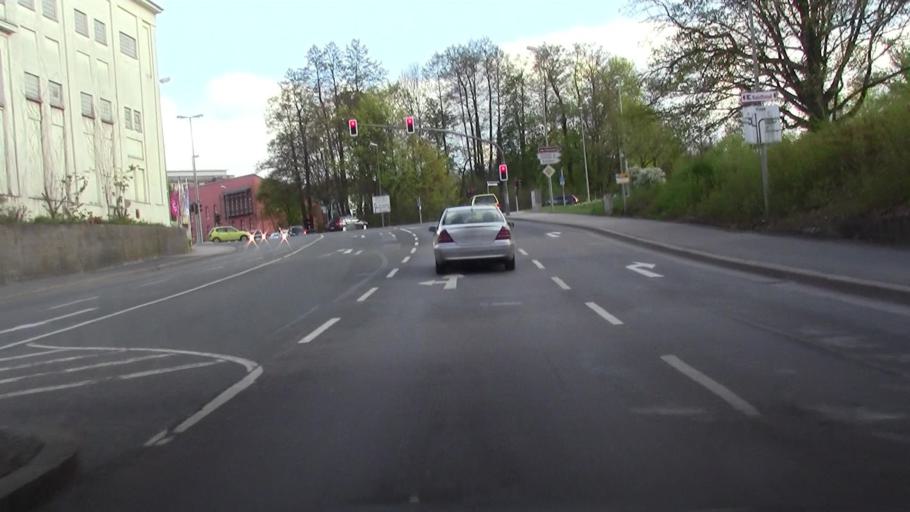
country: DE
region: Bavaria
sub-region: Upper Franconia
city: Kulmbach
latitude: 50.1090
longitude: 11.4489
